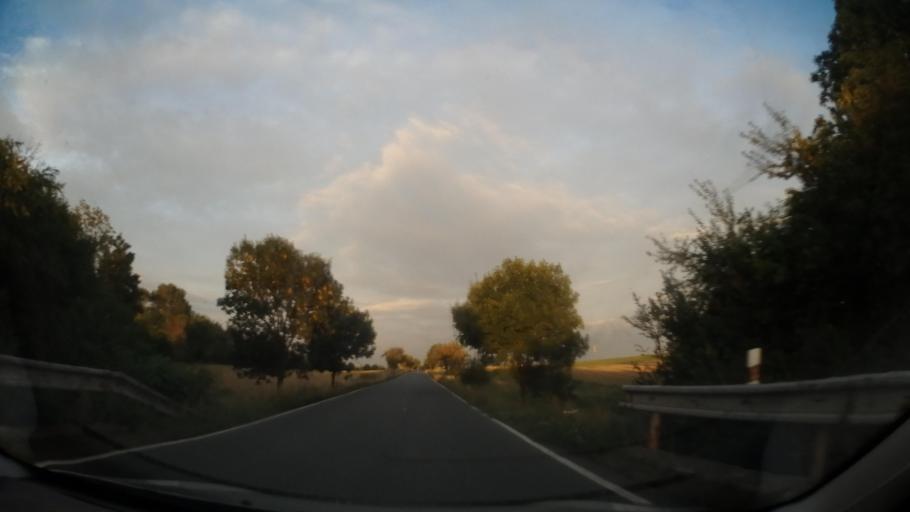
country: CZ
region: Central Bohemia
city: Loucen
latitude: 50.2385
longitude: 15.0018
